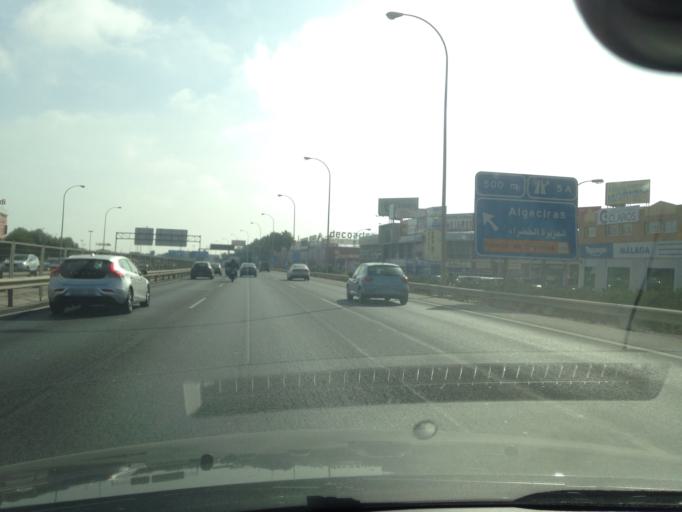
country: ES
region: Andalusia
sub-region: Provincia de Malaga
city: Malaga
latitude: 36.6931
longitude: -4.4608
